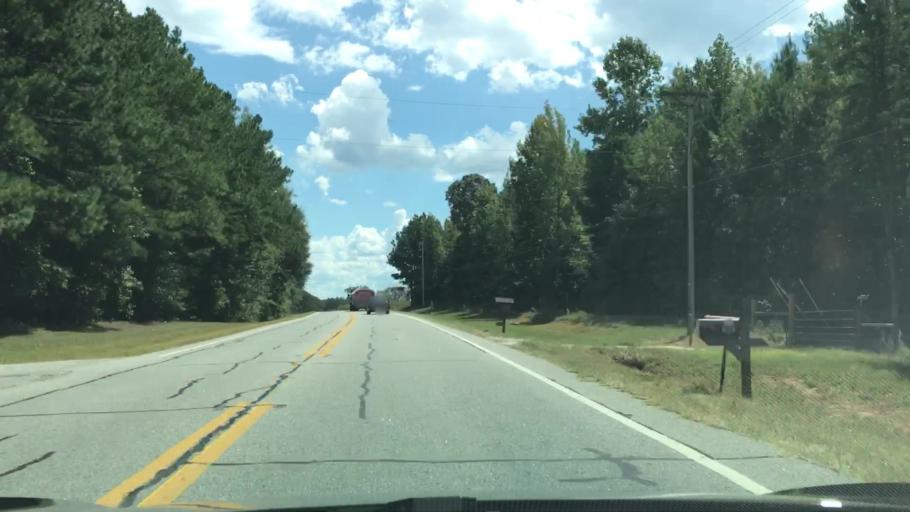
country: US
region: Georgia
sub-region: Oconee County
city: Watkinsville
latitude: 33.7603
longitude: -83.3082
